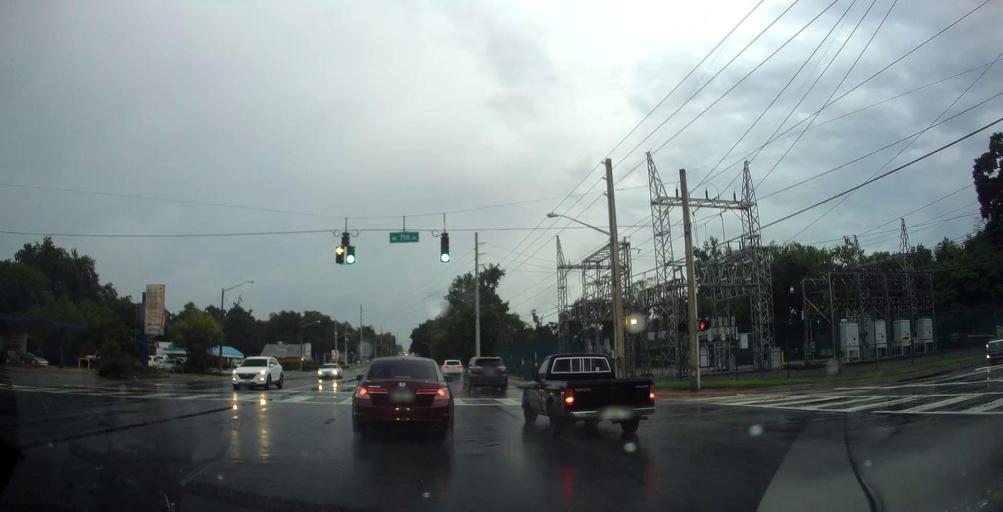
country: US
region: Florida
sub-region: Marion County
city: Ocala
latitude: 29.1938
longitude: -82.0869
